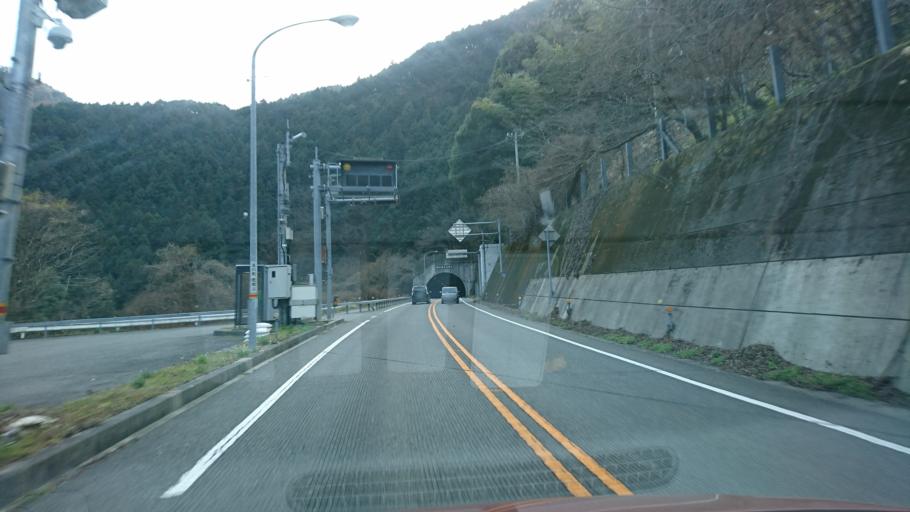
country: JP
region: Ehime
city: Hojo
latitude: 33.9547
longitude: 132.9116
